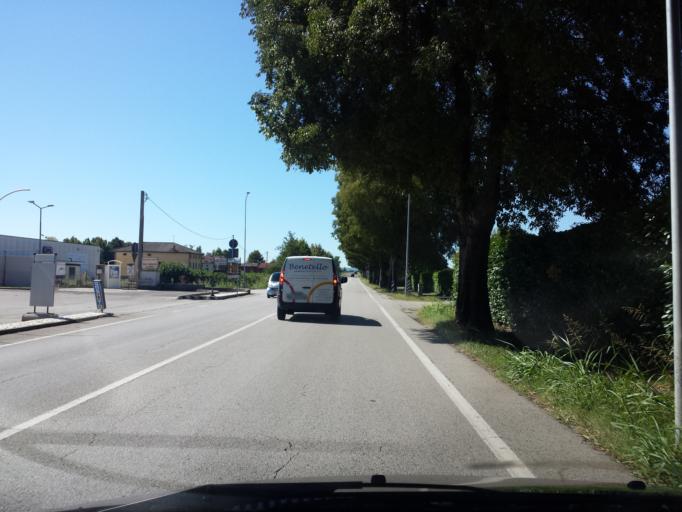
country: IT
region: Veneto
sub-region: Provincia di Vicenza
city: Dueville
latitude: 45.6202
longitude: 11.5682
